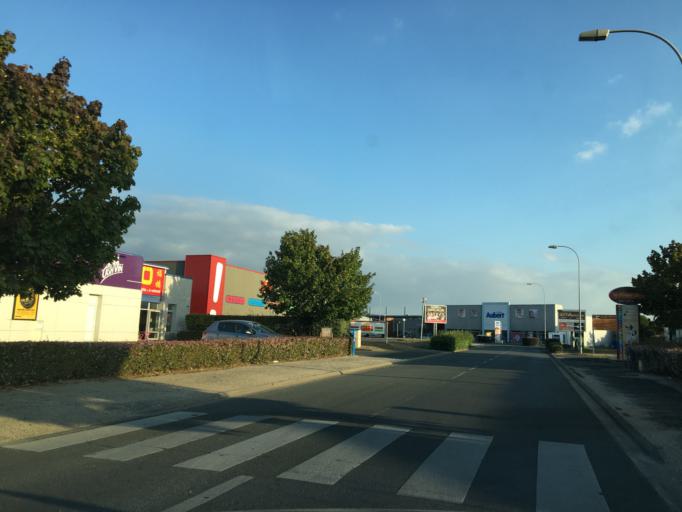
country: FR
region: Poitou-Charentes
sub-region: Departement de la Charente-Maritime
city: Angoulins
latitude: 46.1059
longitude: -1.1005
